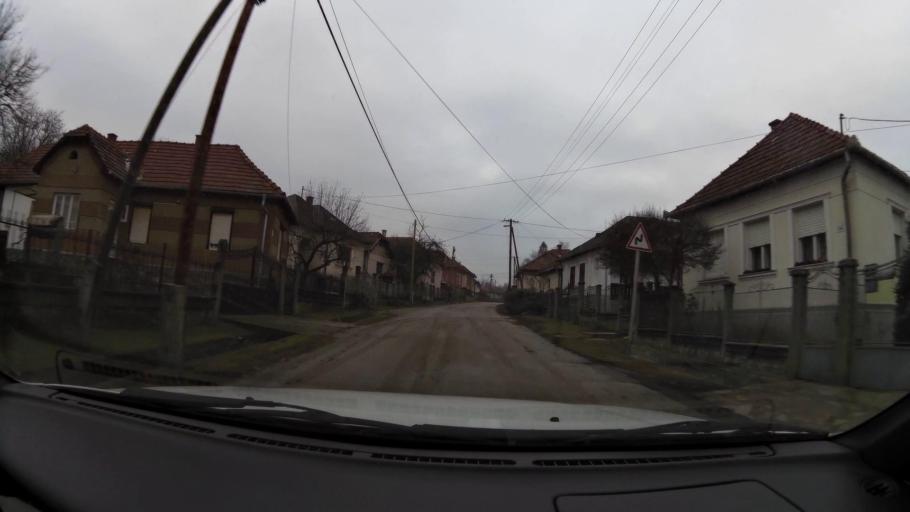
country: HU
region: Borsod-Abauj-Zemplen
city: Rudabanya
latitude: 48.4093
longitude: 20.6558
